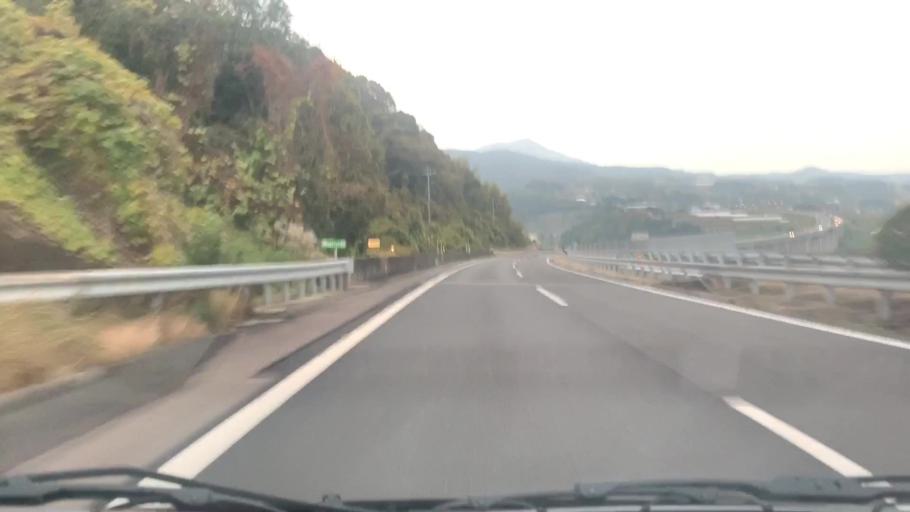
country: JP
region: Nagasaki
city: Omura
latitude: 33.0268
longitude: 129.9373
